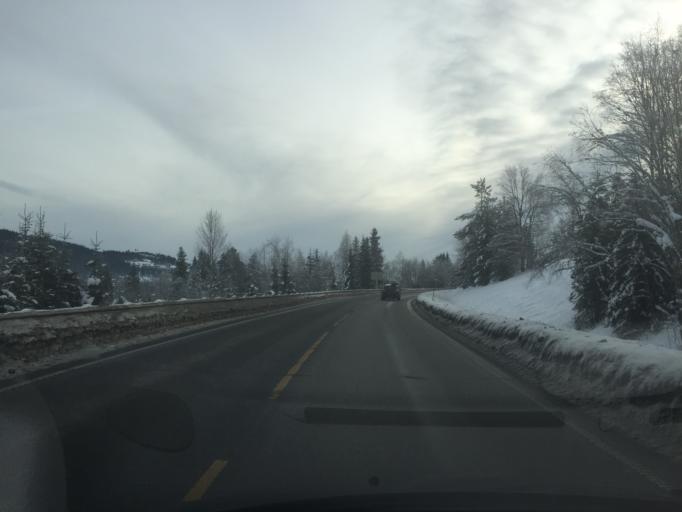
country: NO
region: Hedmark
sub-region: Trysil
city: Innbygda
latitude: 61.2699
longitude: 12.3026
